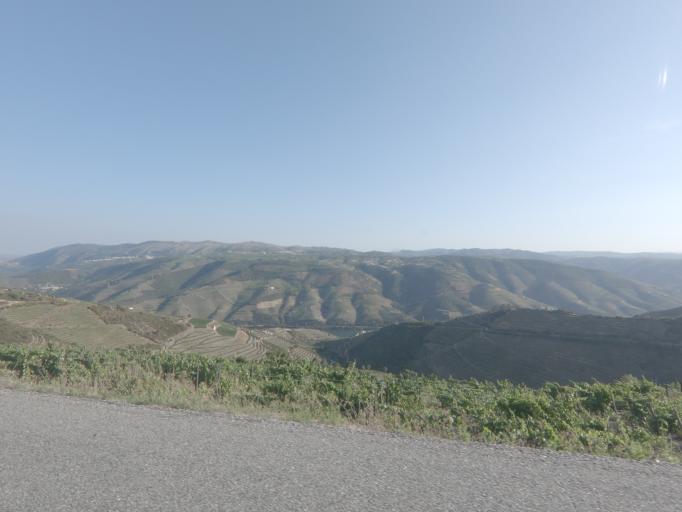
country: PT
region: Vila Real
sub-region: Sabrosa
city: Vilela
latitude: 41.1741
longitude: -7.5960
